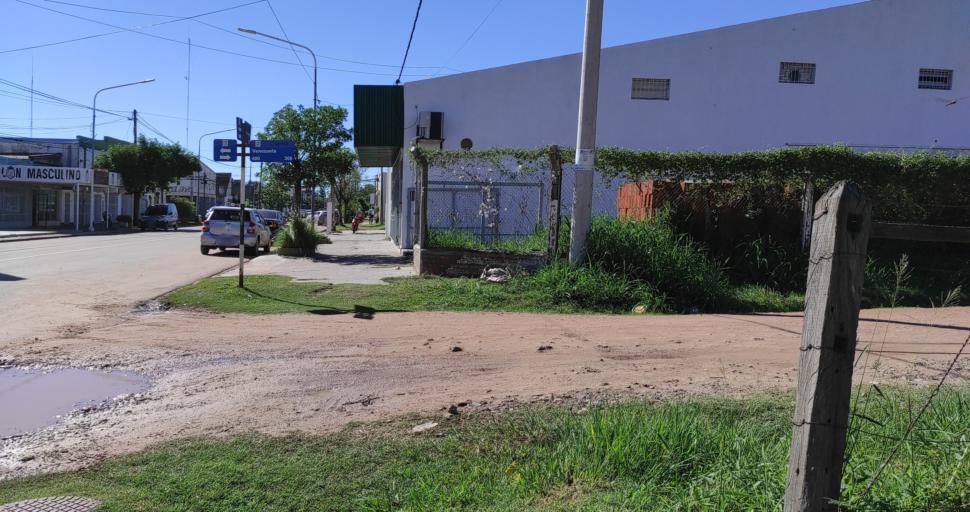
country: AR
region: Chaco
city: Charata
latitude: -27.2244
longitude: -61.1811
